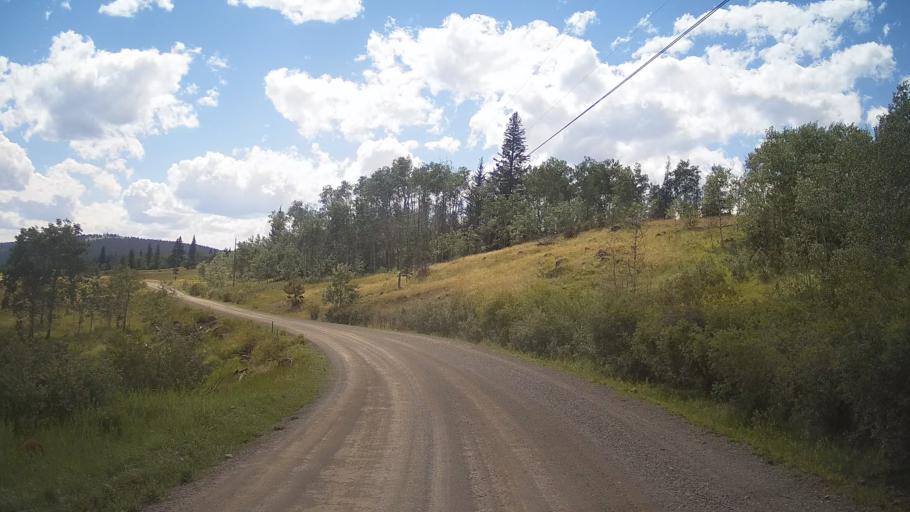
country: CA
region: British Columbia
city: Lillooet
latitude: 51.3262
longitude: -121.9792
